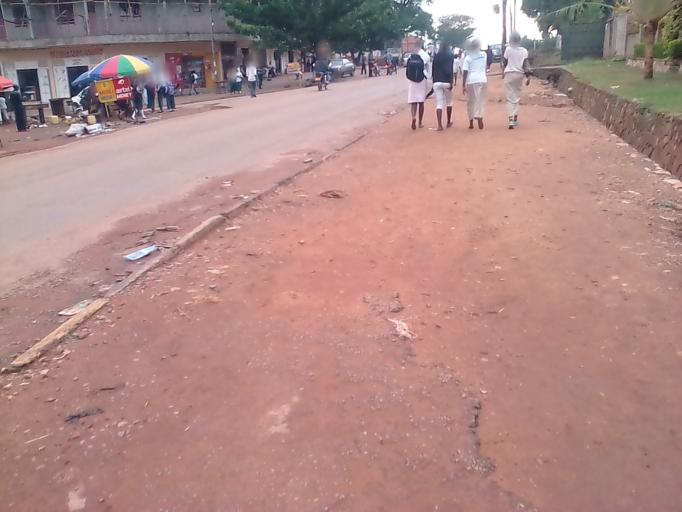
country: UG
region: Eastern Region
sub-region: Mbale District
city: Mbale
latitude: 1.0770
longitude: 34.1687
